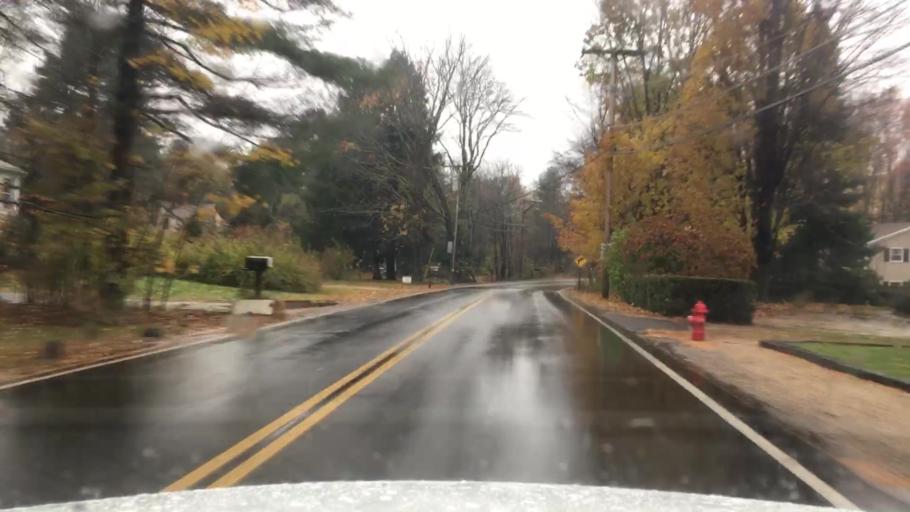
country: US
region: New Hampshire
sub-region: Strafford County
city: Rochester
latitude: 43.3260
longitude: -70.9560
